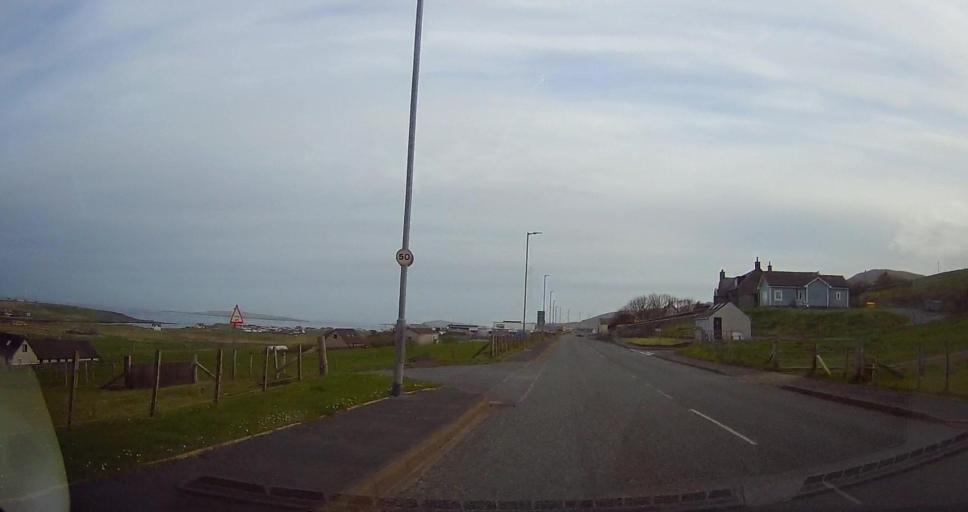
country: GB
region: Scotland
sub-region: Shetland Islands
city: Sandwick
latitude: 60.0483
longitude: -1.2276
